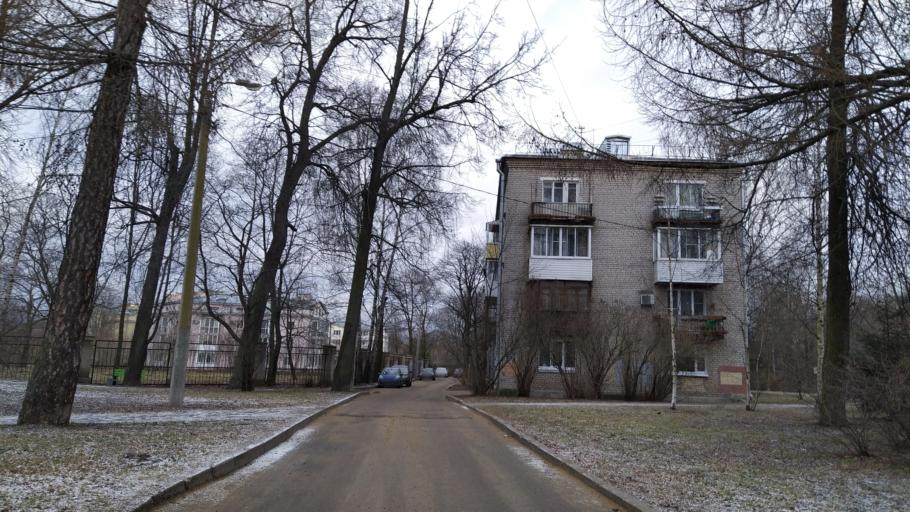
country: RU
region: St.-Petersburg
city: Pushkin
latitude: 59.7223
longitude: 30.4187
